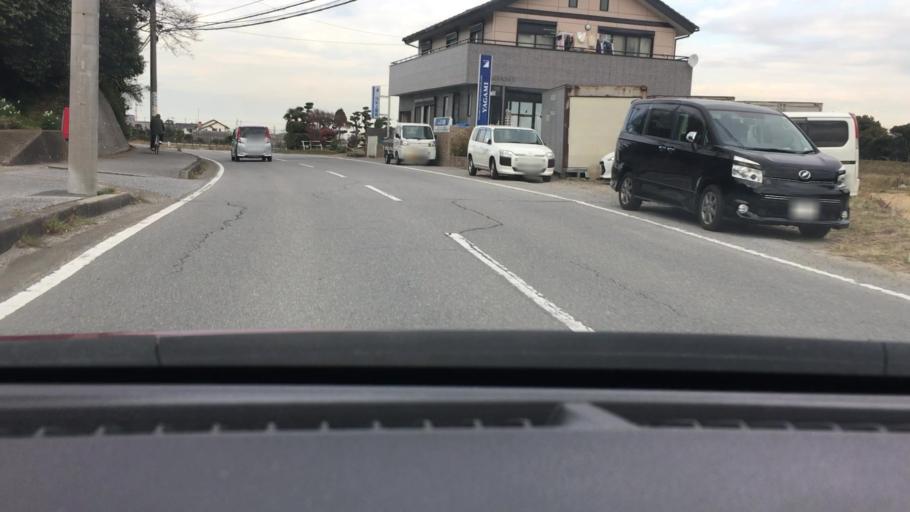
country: JP
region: Chiba
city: Ichihara
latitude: 35.4736
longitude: 140.0635
